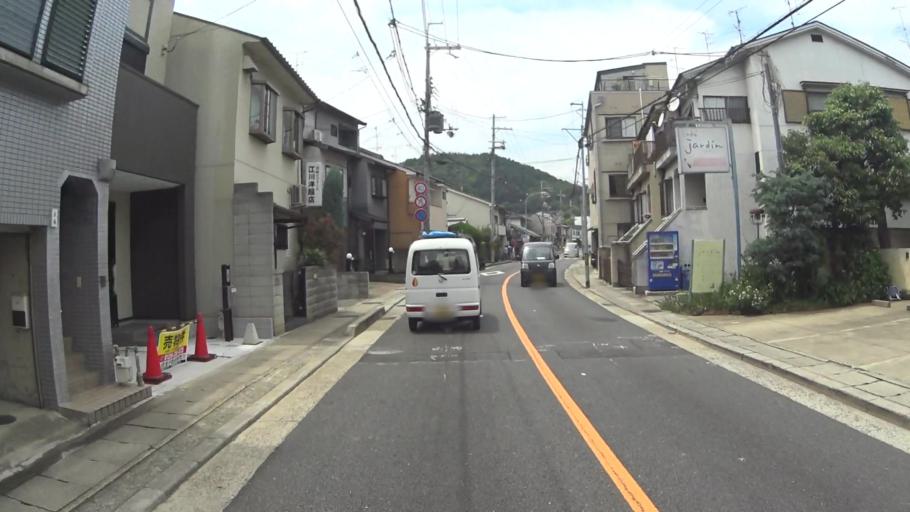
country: JP
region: Kyoto
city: Kyoto
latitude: 35.0300
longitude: 135.7062
